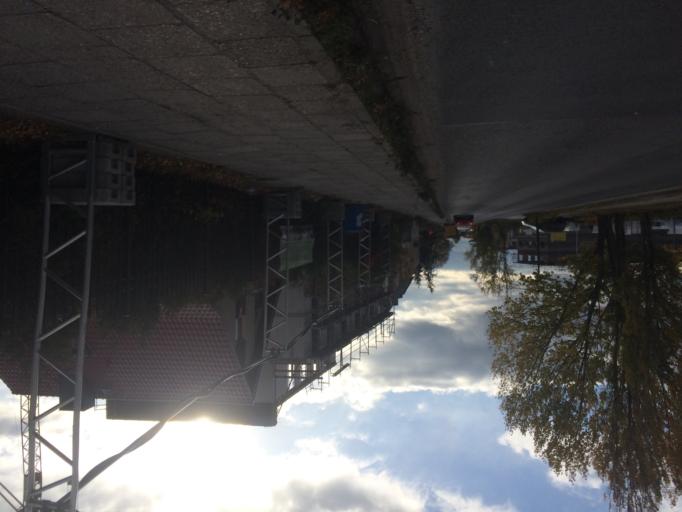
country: DE
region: Berlin
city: Buchholz
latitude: 52.6112
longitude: 13.4308
